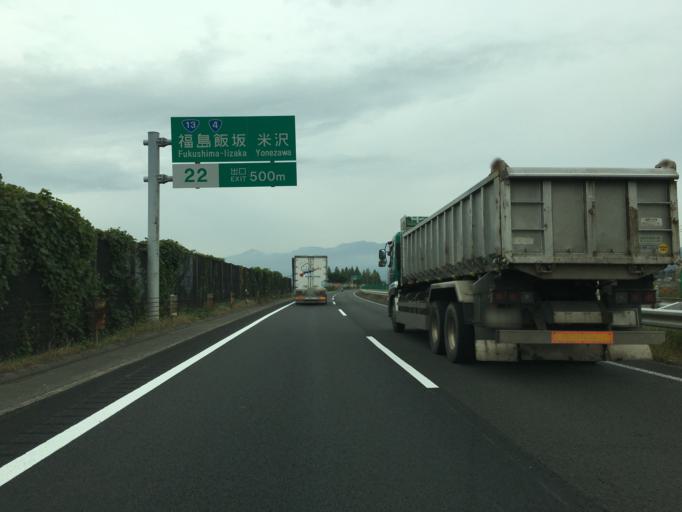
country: JP
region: Fukushima
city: Fukushima-shi
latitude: 37.8040
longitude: 140.4615
